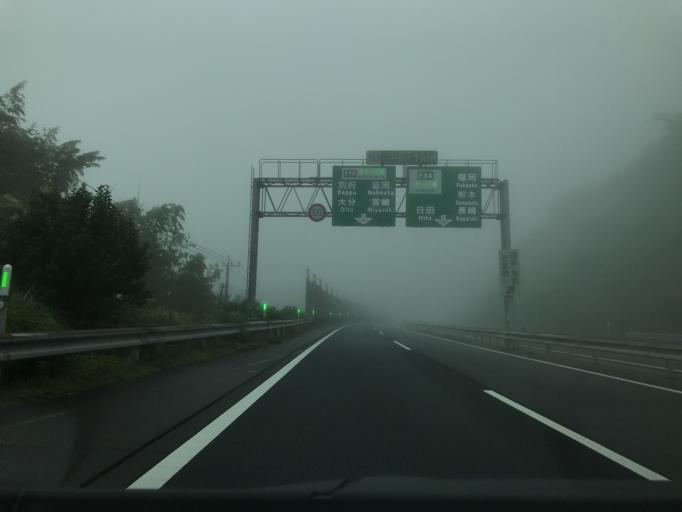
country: JP
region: Oita
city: Hiji
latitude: 33.3610
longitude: 131.4509
